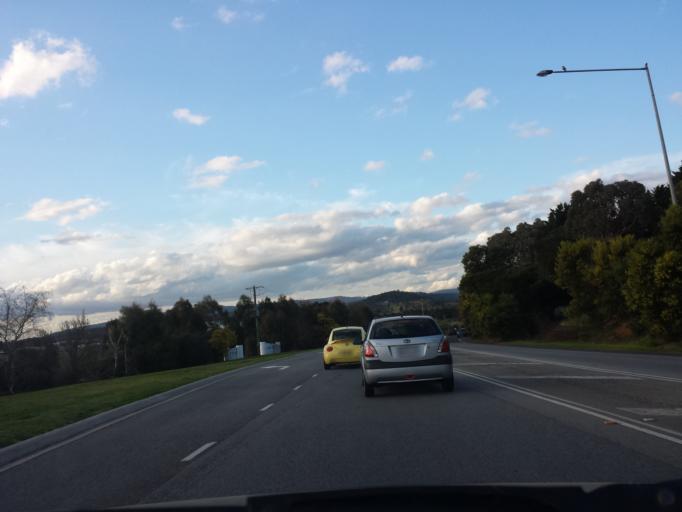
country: AU
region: Victoria
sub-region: Casey
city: Narre Warren North
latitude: -37.9801
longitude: 145.3108
